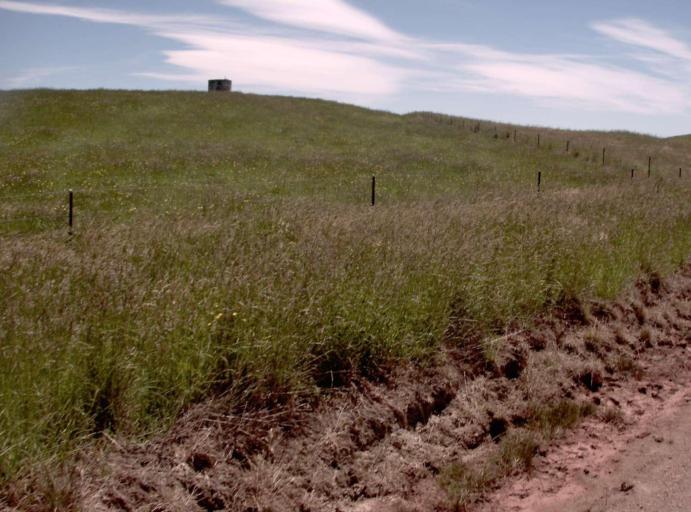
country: AU
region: New South Wales
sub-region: Snowy River
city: Jindabyne
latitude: -37.0929
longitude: 148.2533
